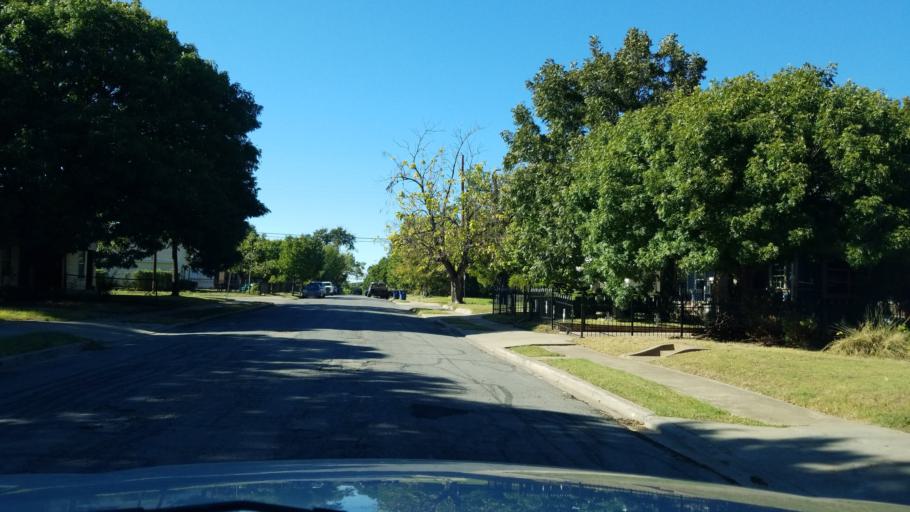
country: US
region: Texas
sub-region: Dallas County
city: Highland Park
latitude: 32.7977
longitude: -96.7456
